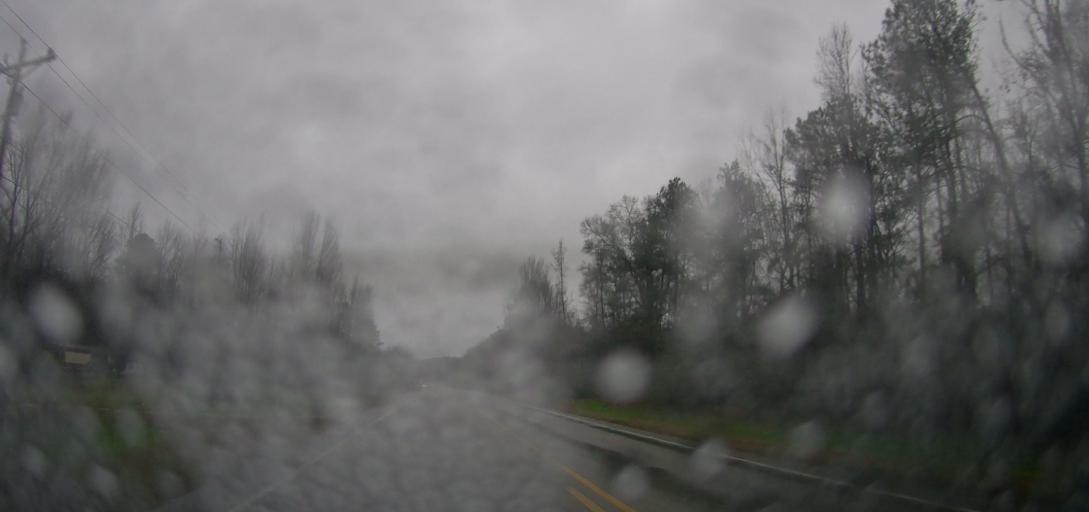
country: US
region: Alabama
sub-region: Autauga County
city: Prattville
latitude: 32.5064
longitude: -86.5862
